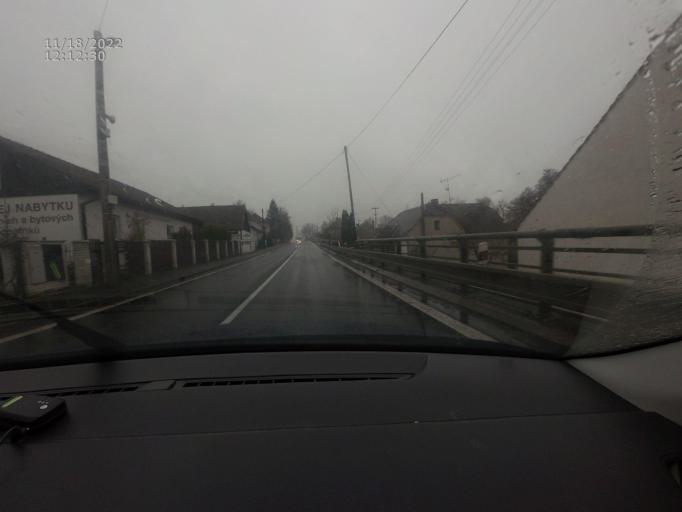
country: CZ
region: Plzensky
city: Blovice
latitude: 49.5447
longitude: 13.5196
